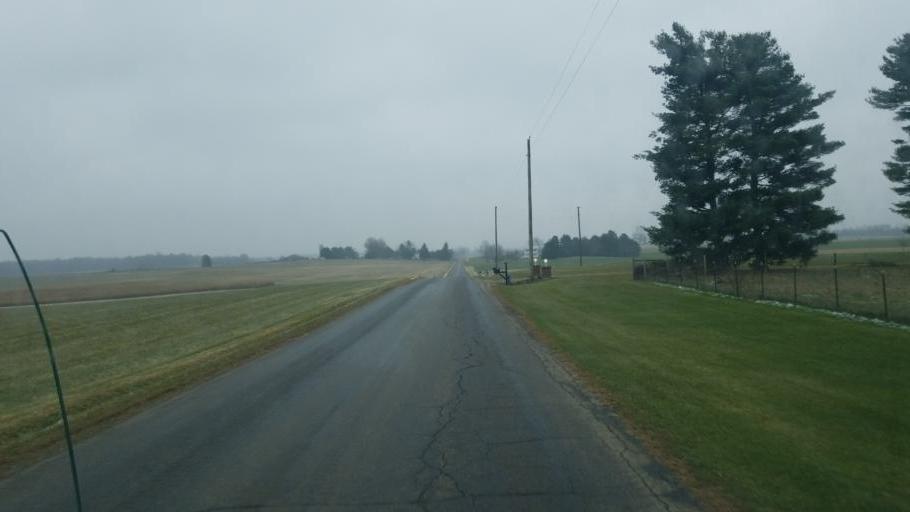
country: US
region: Ohio
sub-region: Huron County
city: Greenwich
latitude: 40.9755
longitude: -82.5411
